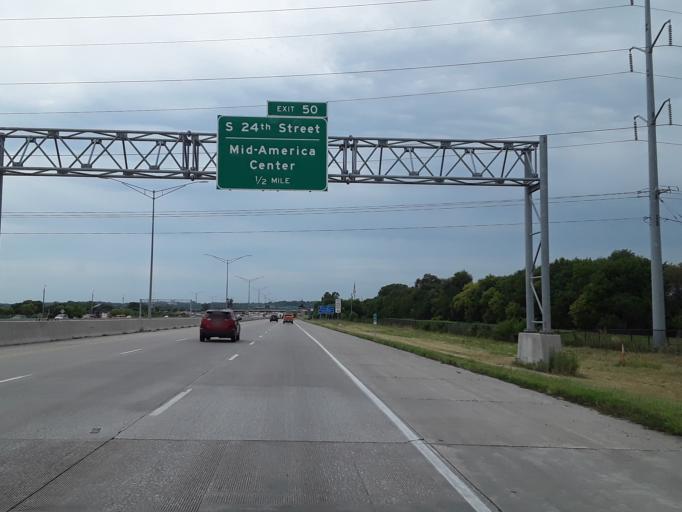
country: US
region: Iowa
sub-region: Pottawattamie County
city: Council Bluffs
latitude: 41.2327
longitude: -95.8654
